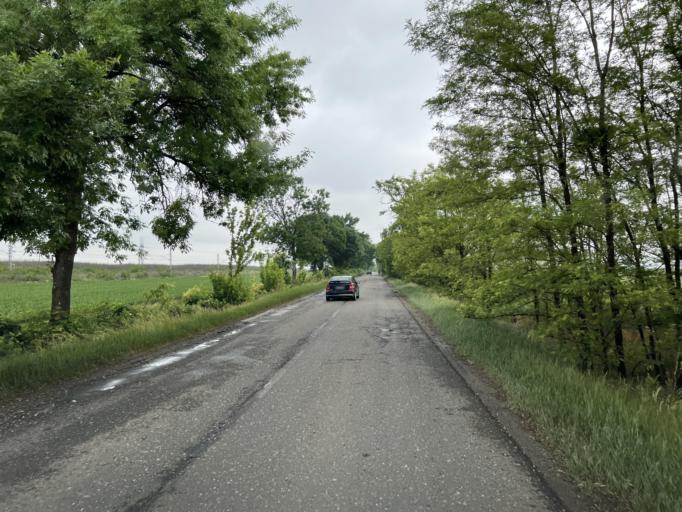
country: HU
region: Pest
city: Tura
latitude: 47.6324
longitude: 19.6305
